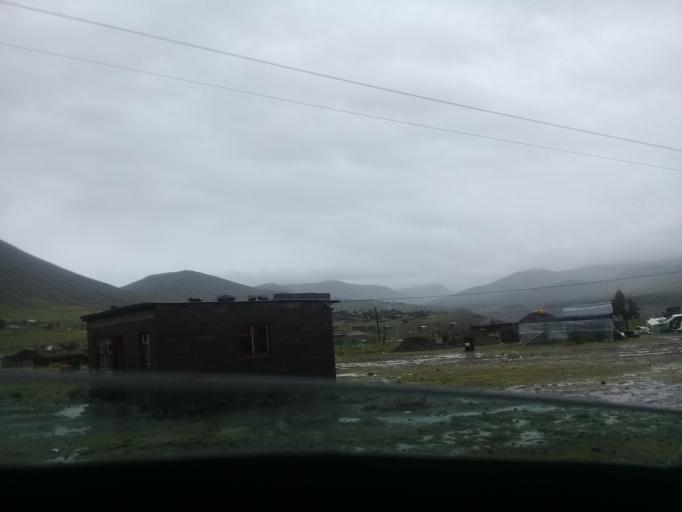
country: LS
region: Mokhotlong
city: Mokhotlong
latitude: -29.3341
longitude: 29.0330
